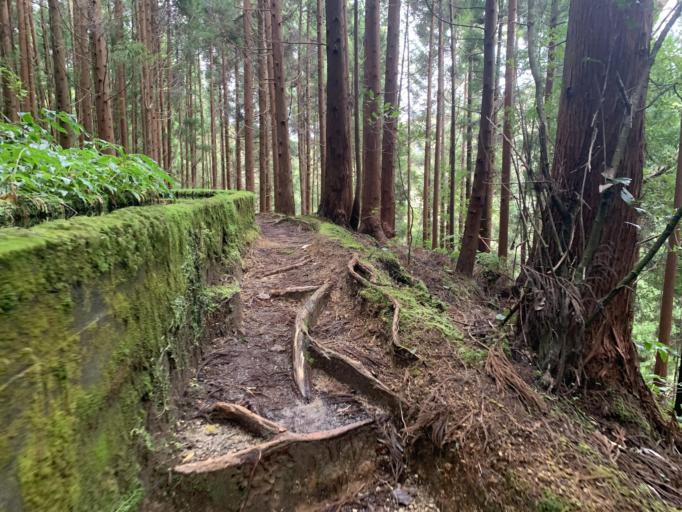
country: PT
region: Azores
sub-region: Vila Franca do Campo
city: Vila Franca do Campo
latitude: 37.7440
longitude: -25.4752
